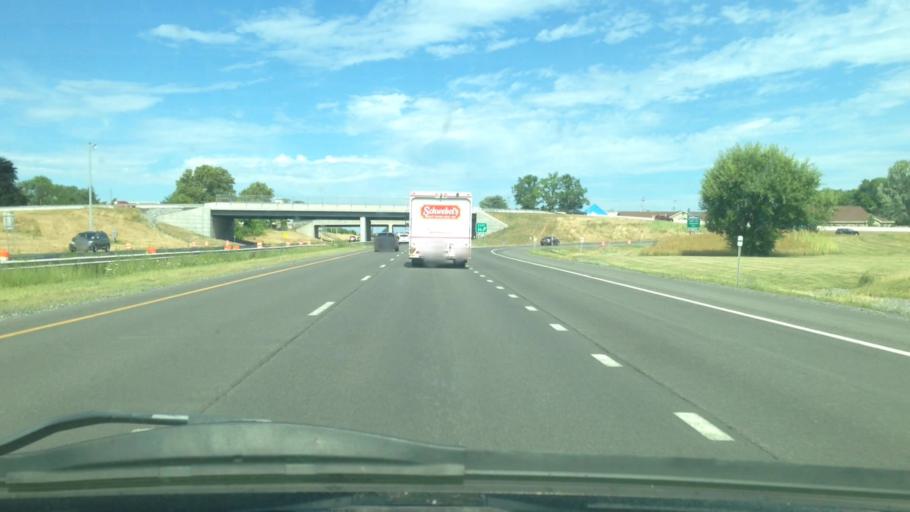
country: US
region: New York
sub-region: Onondaga County
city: Galeville
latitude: 43.0938
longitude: -76.1657
